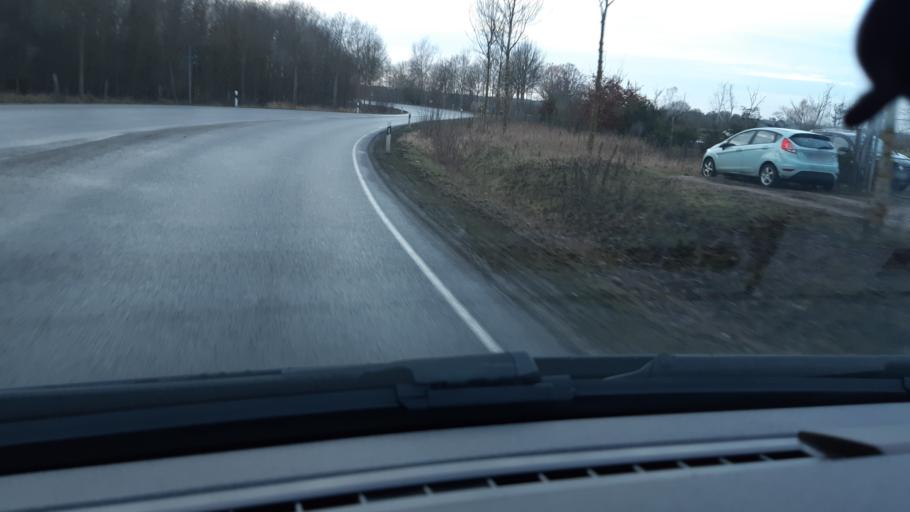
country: DE
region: Brandenburg
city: Leegebruch
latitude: 52.7378
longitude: 13.2024
